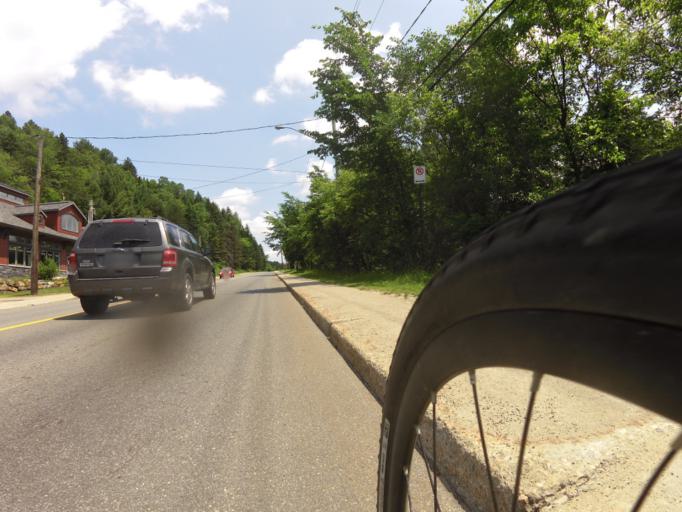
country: CA
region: Quebec
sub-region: Laurentides
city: Mont-Tremblant
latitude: 46.1188
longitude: -74.5864
